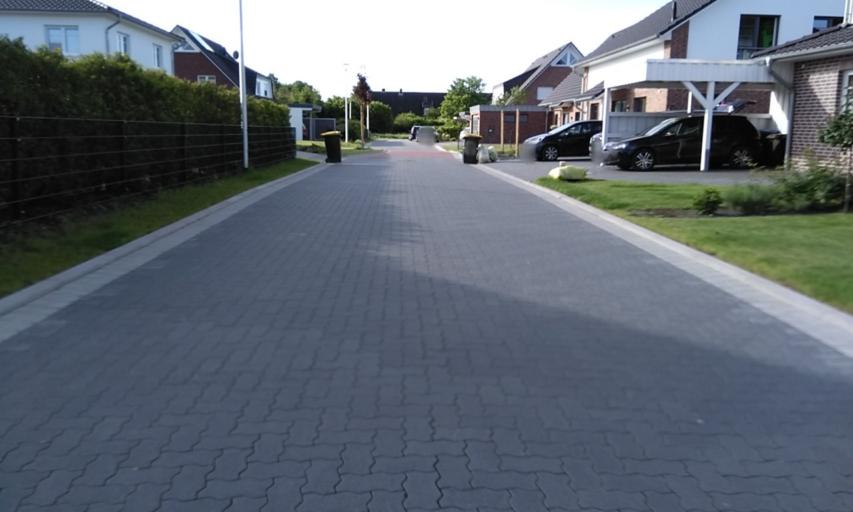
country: DE
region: Lower Saxony
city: Apensen
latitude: 53.4397
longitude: 9.6215
